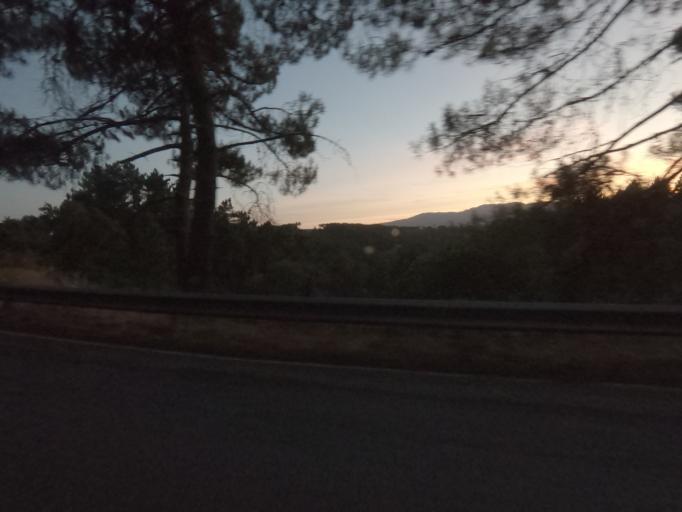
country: PT
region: Vila Real
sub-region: Sabrosa
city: Vilela
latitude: 41.2301
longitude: -7.6772
